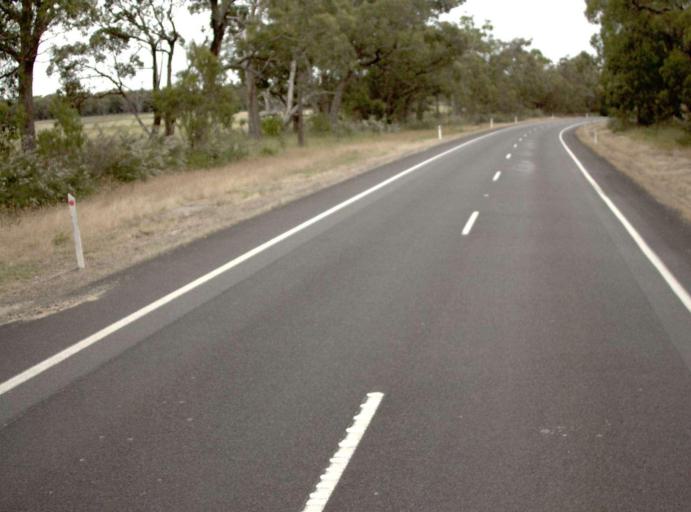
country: AU
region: Victoria
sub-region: Wellington
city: Sale
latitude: -38.3118
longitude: 147.0284
